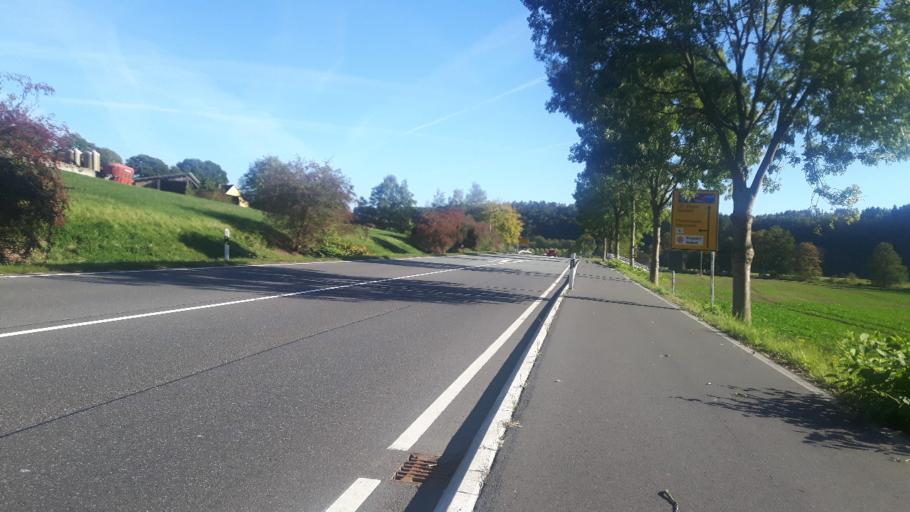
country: DE
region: Rheinland-Pfalz
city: Katzwinkel
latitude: 50.8031
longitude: 7.7996
